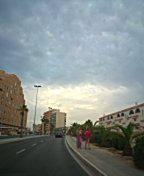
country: ES
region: Murcia
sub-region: Murcia
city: La Manga del Mar Menor
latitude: 37.6911
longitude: -0.7376
